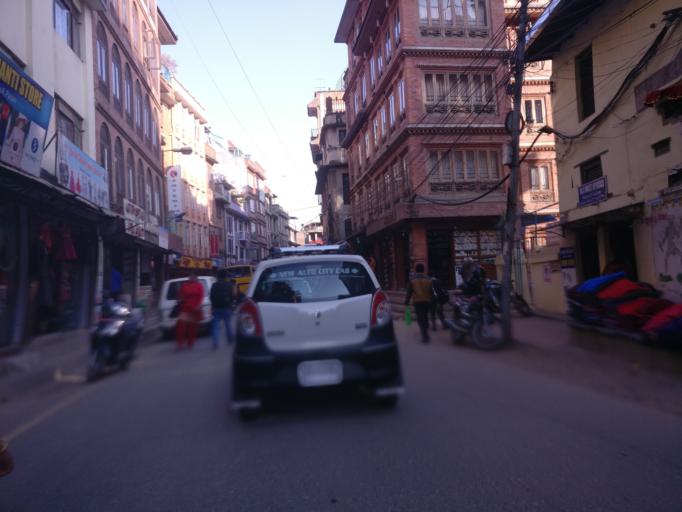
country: NP
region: Central Region
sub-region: Bagmati Zone
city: Patan
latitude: 27.6738
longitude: 85.3230
